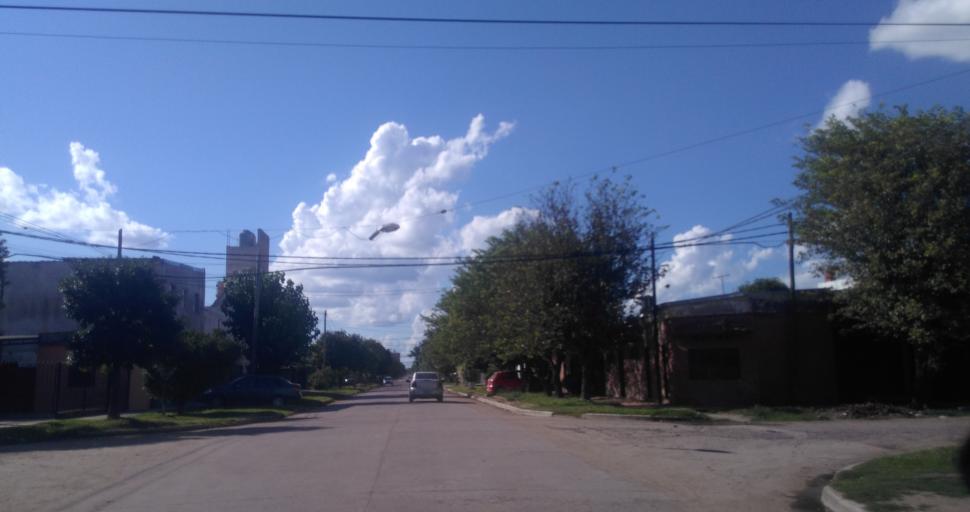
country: AR
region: Chaco
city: Resistencia
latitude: -27.4719
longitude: -58.9700
